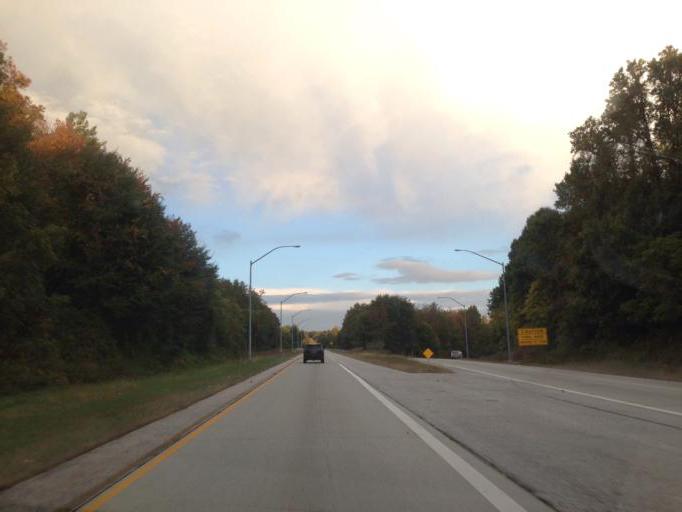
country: US
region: Maryland
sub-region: Baltimore County
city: Owings Mills
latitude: 39.4108
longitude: -76.7852
